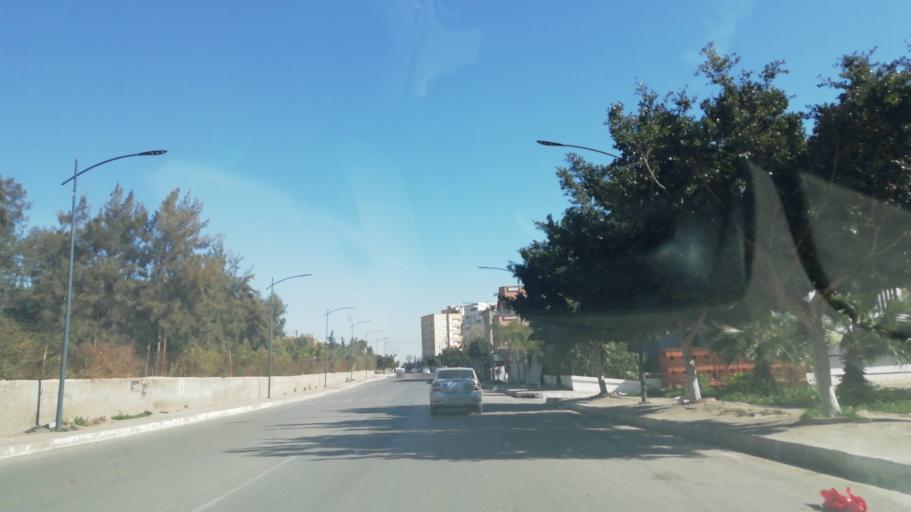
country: DZ
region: Oran
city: Bir el Djir
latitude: 35.7162
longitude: -0.5846
